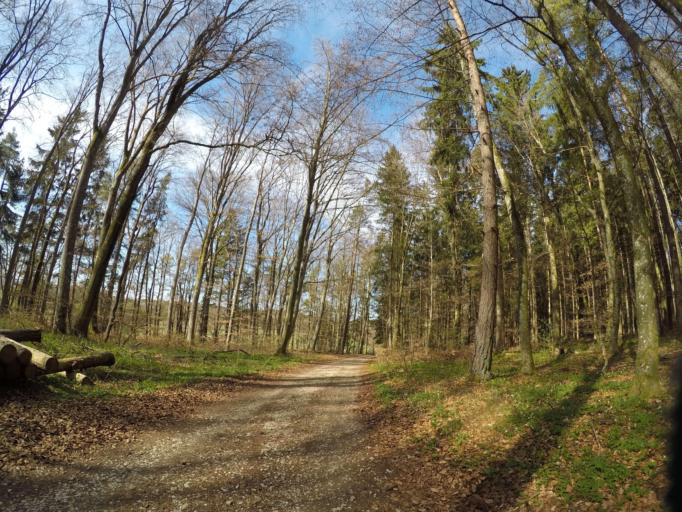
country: DE
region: Baden-Wuerttemberg
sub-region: Tuebingen Region
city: Mehrstetten
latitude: 48.3264
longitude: 9.5859
